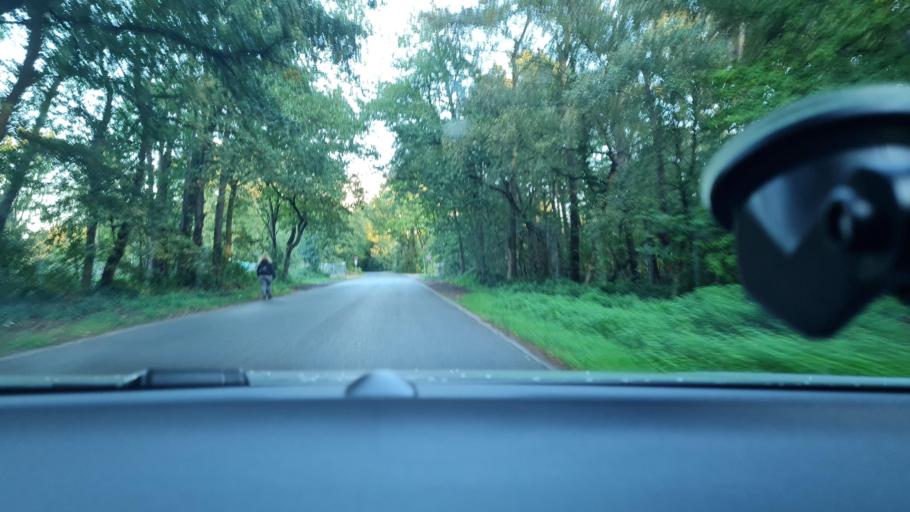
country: DE
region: North Rhine-Westphalia
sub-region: Regierungsbezirk Dusseldorf
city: Voerde
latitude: 51.5928
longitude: 6.7203
